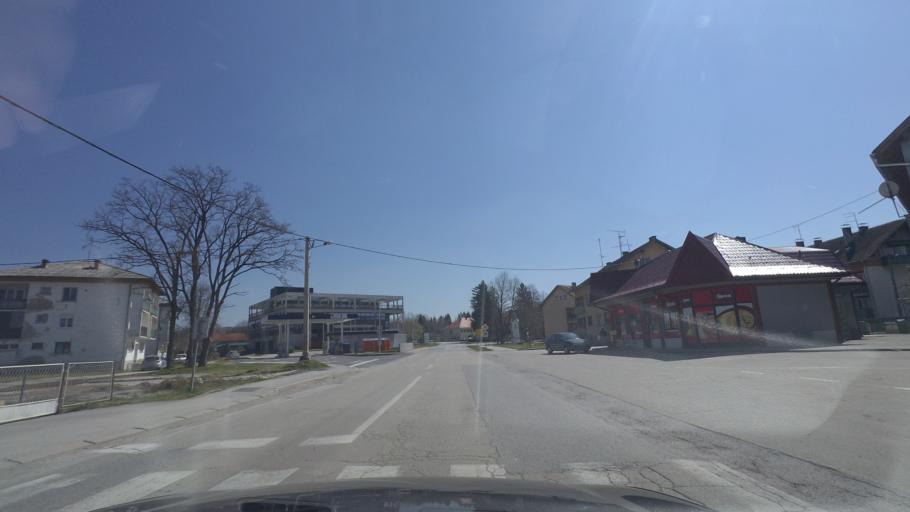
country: HR
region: Karlovacka
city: Vojnic
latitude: 45.3267
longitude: 15.6949
